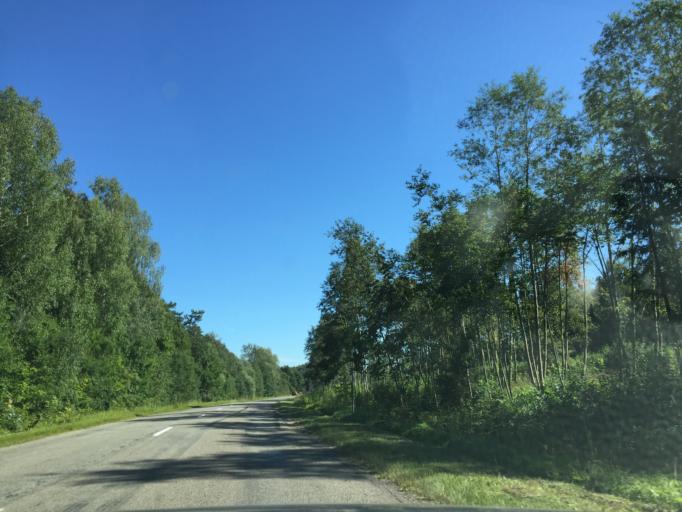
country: LV
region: Akniste
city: Akniste
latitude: 56.1119
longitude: 25.8447
